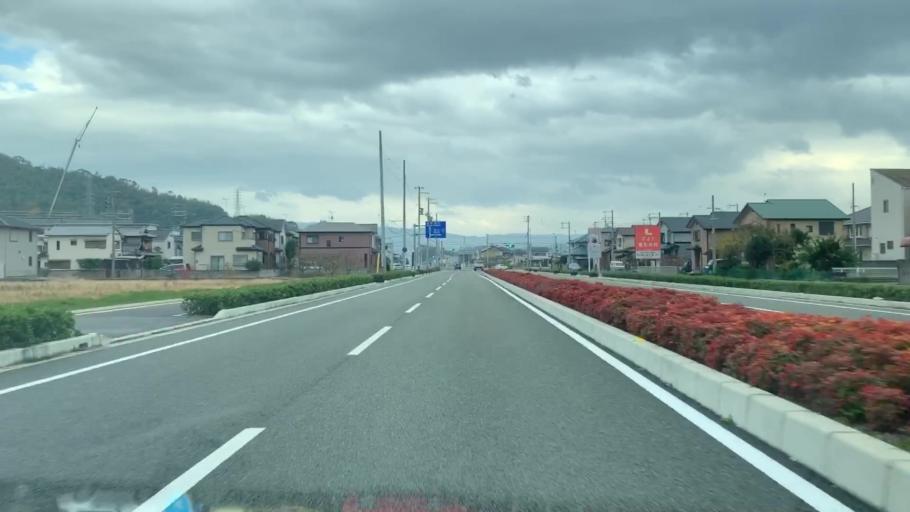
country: JP
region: Wakayama
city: Wakayama-shi
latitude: 34.2184
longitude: 135.2074
